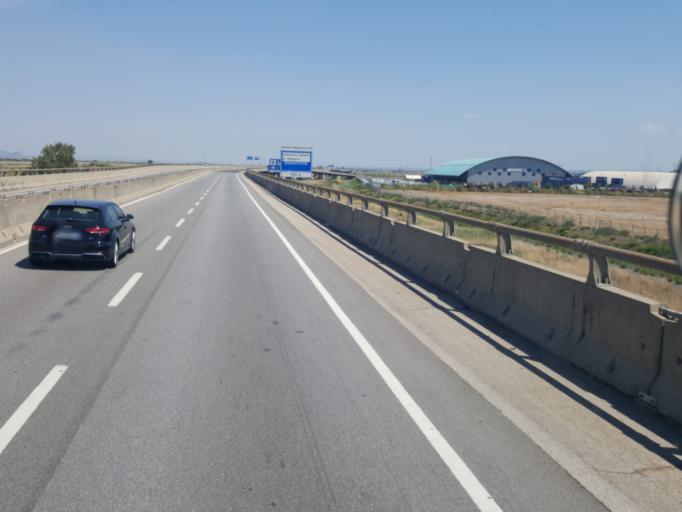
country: IT
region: Tuscany
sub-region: Provincia di Livorno
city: Guasticce
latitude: 43.6081
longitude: 10.3977
